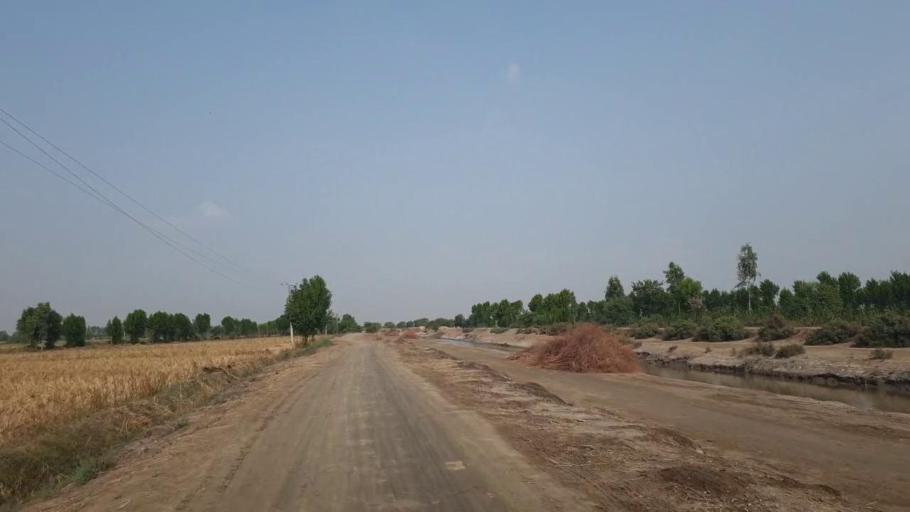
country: PK
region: Sindh
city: Badin
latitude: 24.7511
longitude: 68.7620
